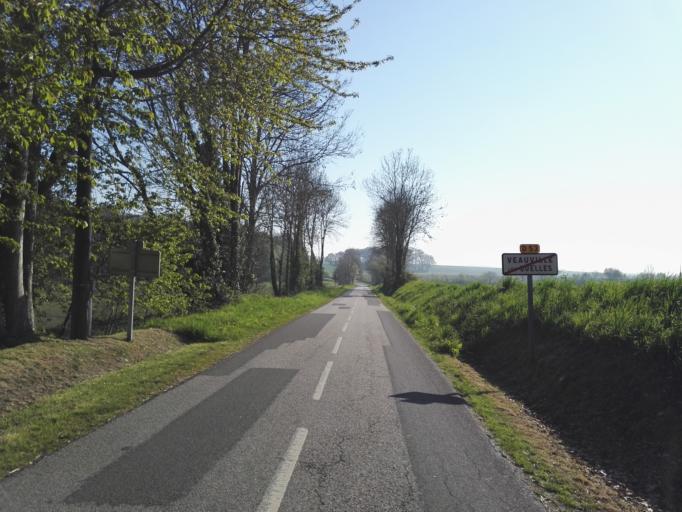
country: FR
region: Haute-Normandie
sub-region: Departement de la Seine-Maritime
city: Doudeville
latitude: 49.7391
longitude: 0.7134
